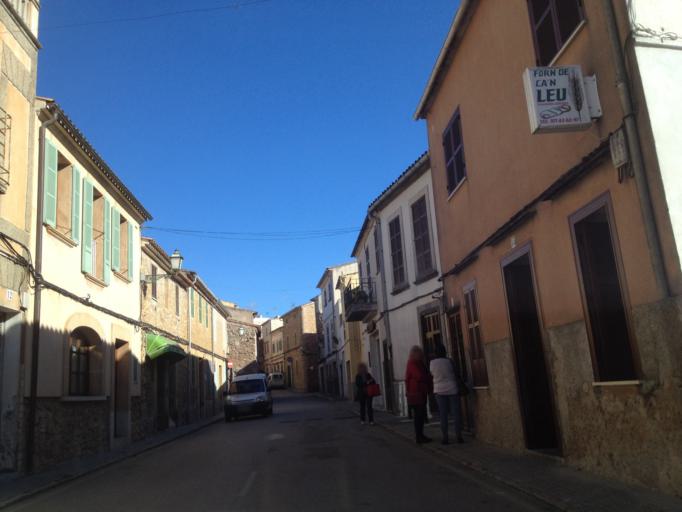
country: ES
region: Balearic Islands
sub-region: Illes Balears
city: Arta
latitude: 39.6939
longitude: 3.3480
